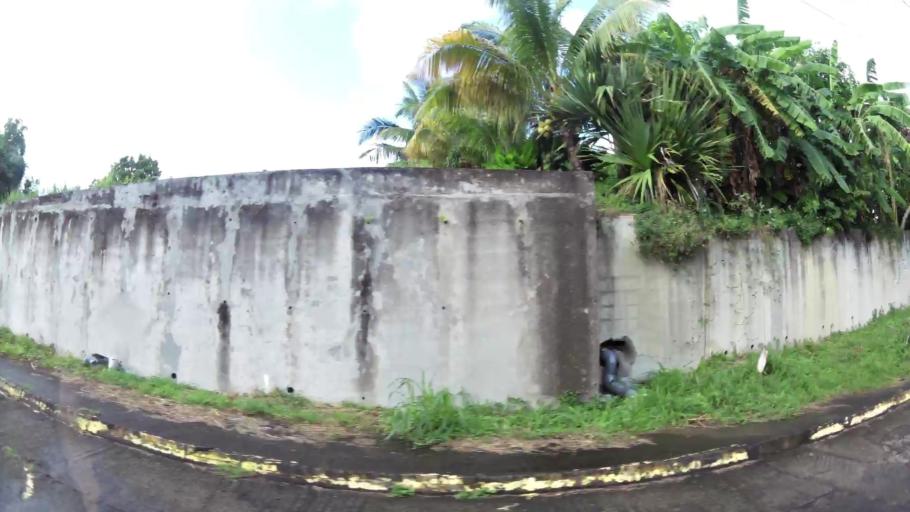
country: MQ
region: Martinique
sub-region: Martinique
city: Les Trois-Ilets
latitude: 14.5451
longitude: -61.0486
